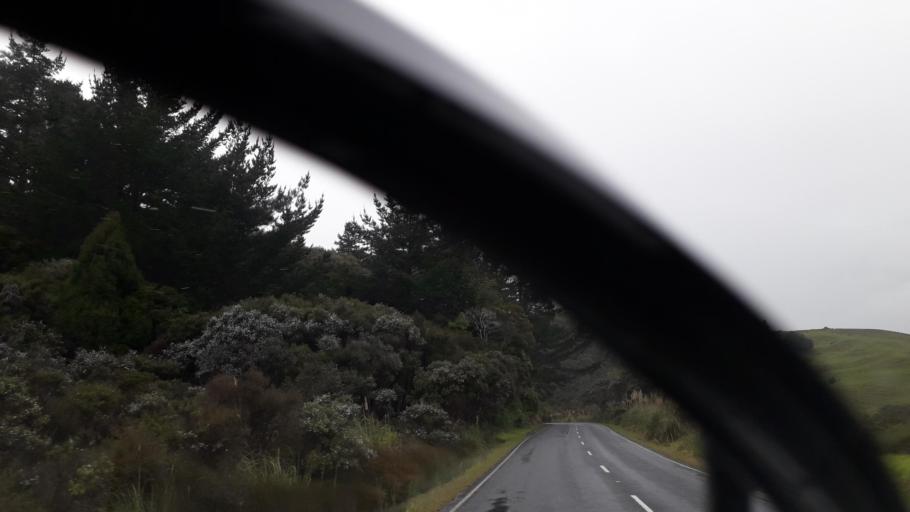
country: NZ
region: Northland
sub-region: Far North District
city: Kaitaia
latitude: -35.3628
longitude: 173.4707
